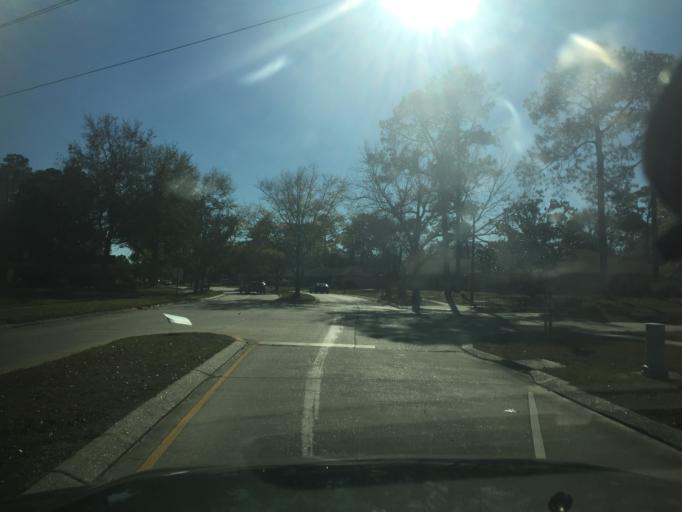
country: US
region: Louisiana
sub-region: Saint Tammany Parish
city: Slidell
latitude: 30.2908
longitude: -89.7582
